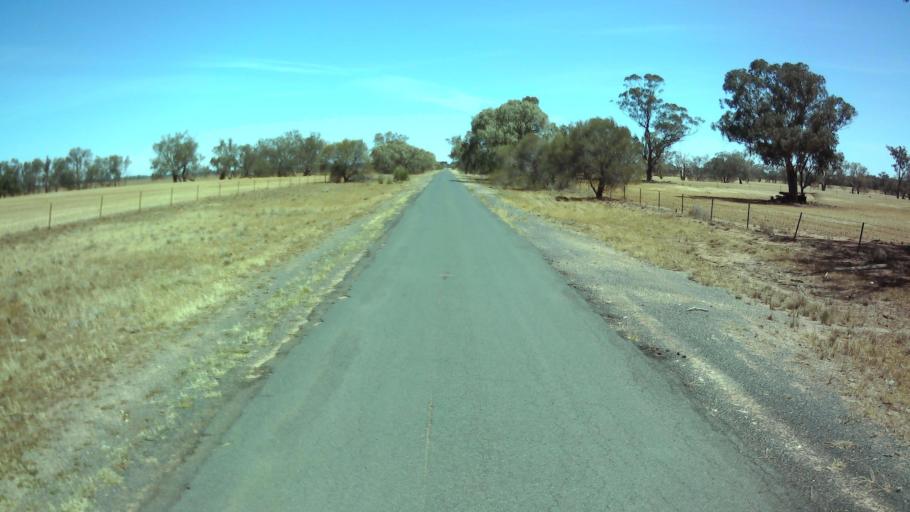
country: AU
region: New South Wales
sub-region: Weddin
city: Grenfell
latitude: -33.8469
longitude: 147.6963
